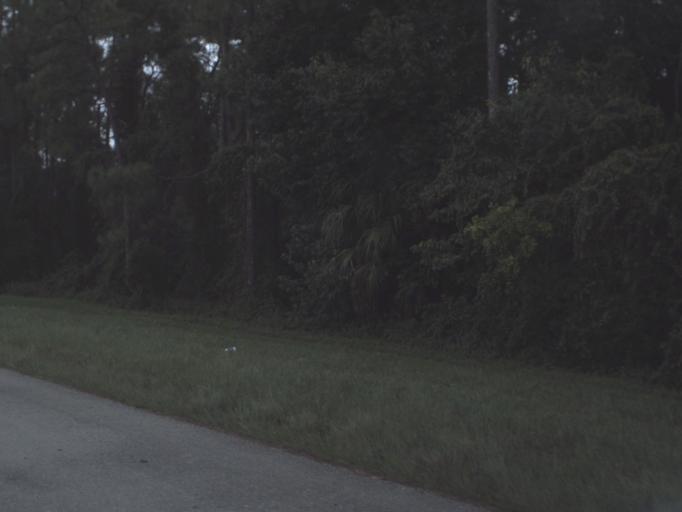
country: US
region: Florida
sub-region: Collier County
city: Vineyards
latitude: 26.2290
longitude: -81.7363
